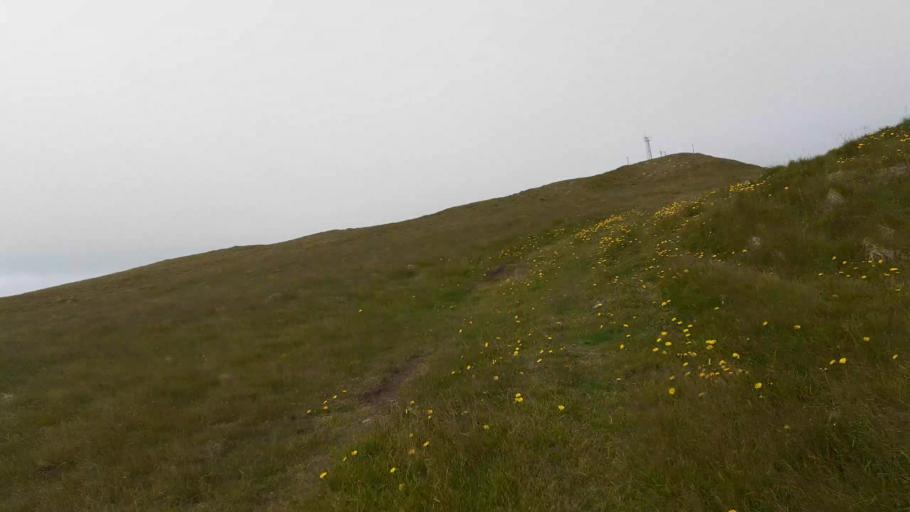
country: IS
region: Northeast
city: Dalvik
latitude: 66.5427
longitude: -17.9922
